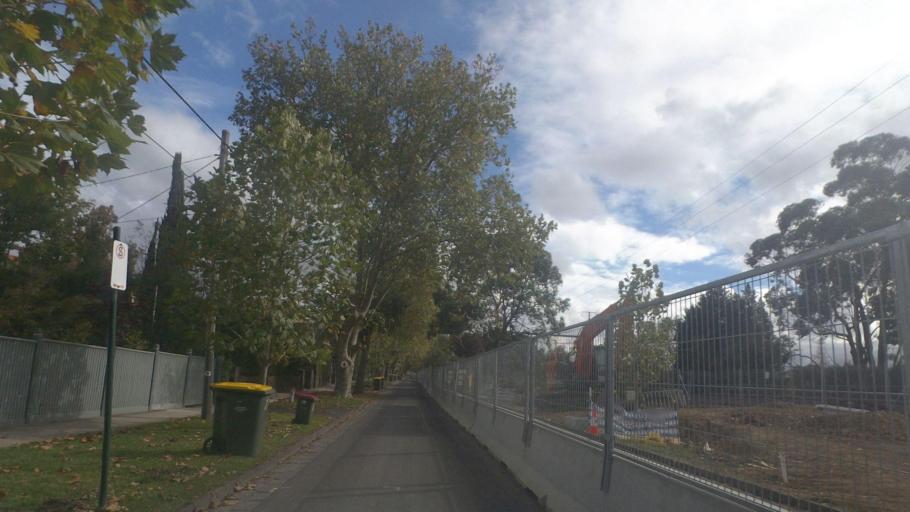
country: AU
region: Victoria
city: Mont Albert
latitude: -37.8185
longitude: 145.1118
